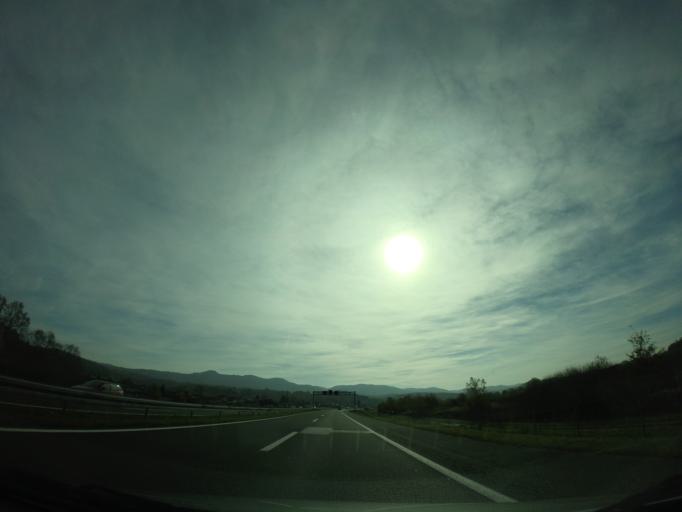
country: HR
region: Varazdinska
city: Ljubescica
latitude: 46.1622
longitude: 16.3752
